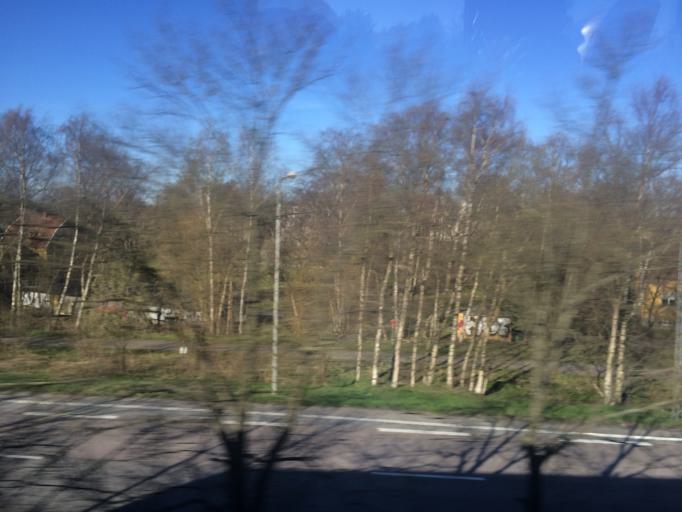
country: SE
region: Vaestra Goetaland
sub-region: Goteborg
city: Majorna
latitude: 57.7030
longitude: 11.8930
